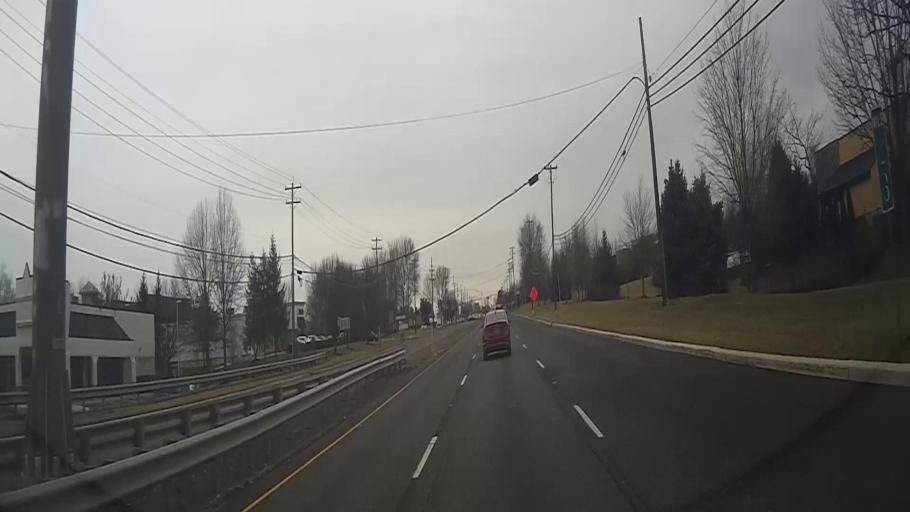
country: US
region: New Jersey
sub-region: Burlington County
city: Marlton
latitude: 39.8785
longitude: -74.9219
